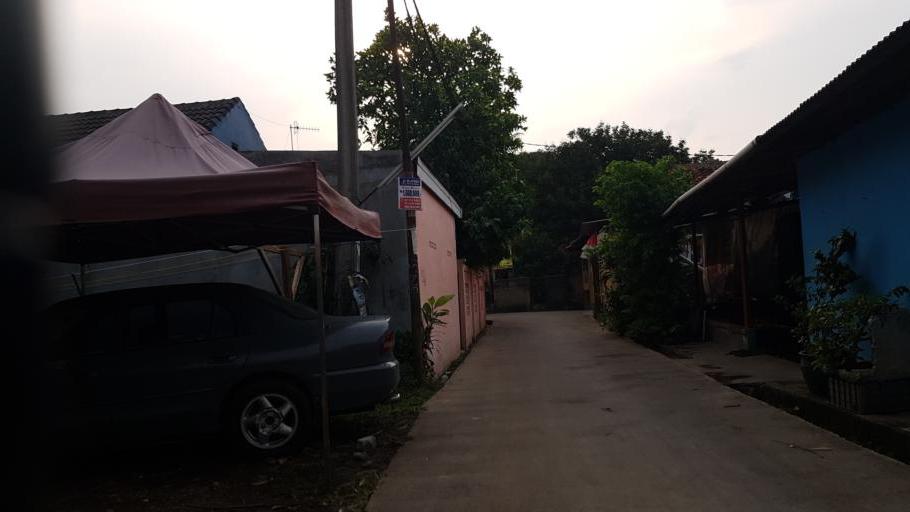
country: ID
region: West Java
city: Depok
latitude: -6.3927
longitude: 106.7994
